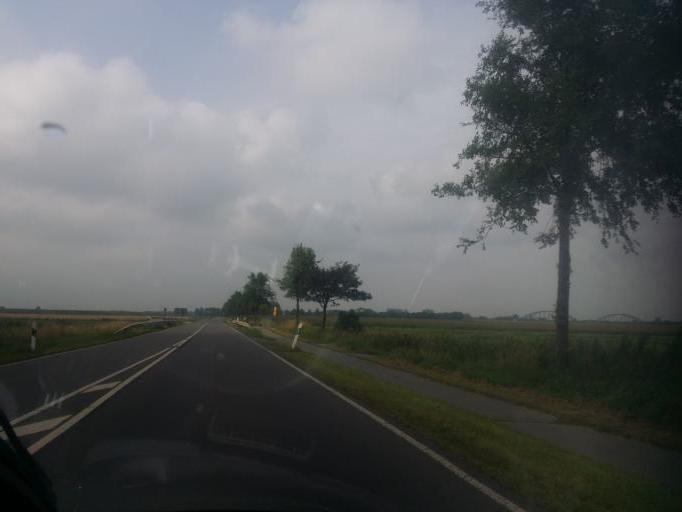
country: DE
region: Schleswig-Holstein
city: Sankt Annen
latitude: 54.3595
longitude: 9.0944
